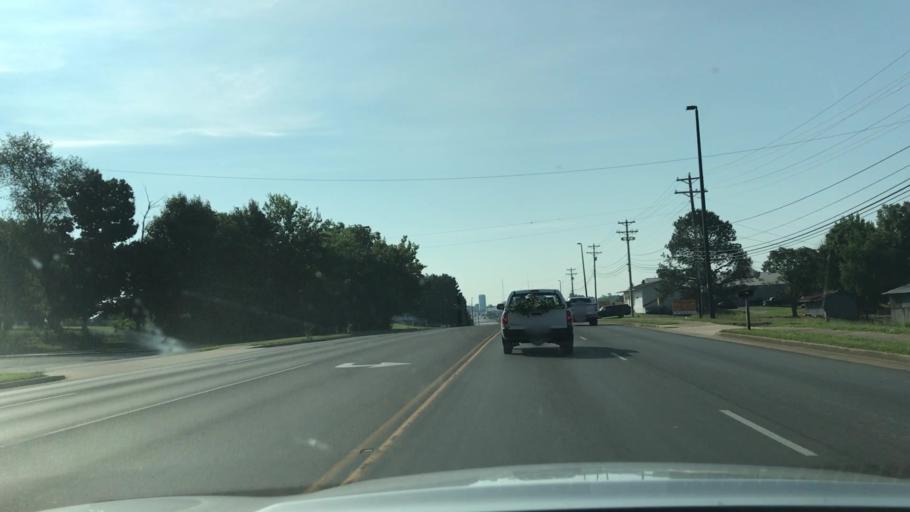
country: US
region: Kentucky
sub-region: Barren County
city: Glasgow
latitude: 37.0070
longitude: -85.9343
